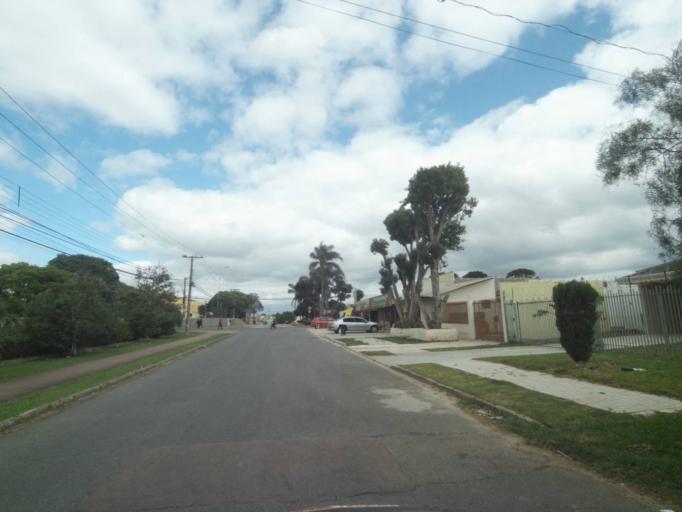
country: BR
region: Parana
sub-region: Sao Jose Dos Pinhais
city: Sao Jose dos Pinhais
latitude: -25.5543
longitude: -49.2540
